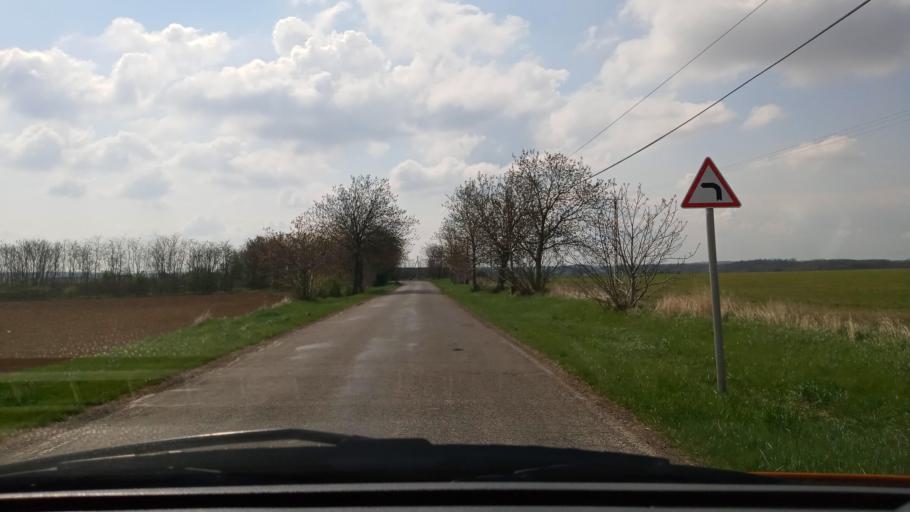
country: HU
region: Baranya
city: Pecsvarad
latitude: 46.0855
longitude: 18.5054
